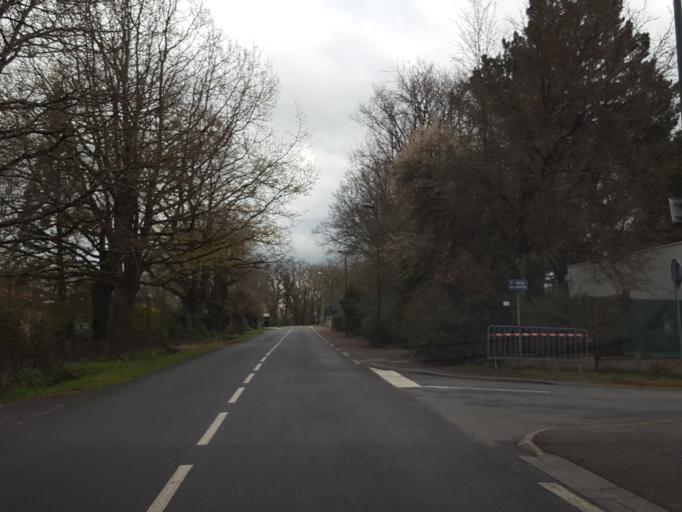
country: FR
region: Pays de la Loire
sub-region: Departement de la Vendee
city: La Roche-sur-Yon
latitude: 46.6740
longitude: -1.3996
